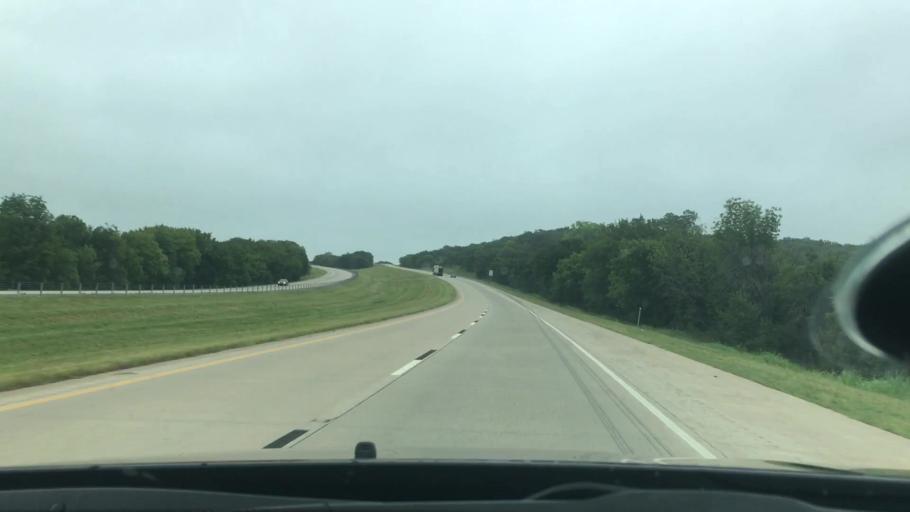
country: US
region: Oklahoma
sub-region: Okmulgee County
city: Henryetta
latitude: 35.4303
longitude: -95.9556
